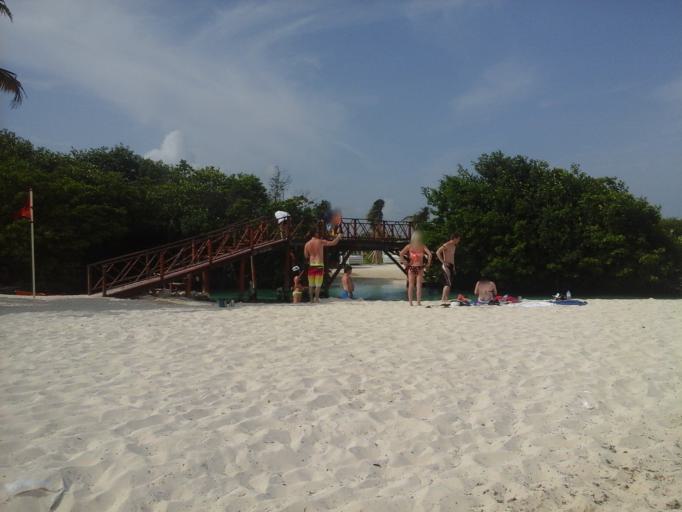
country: MX
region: Quintana Roo
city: Playa del Carmen
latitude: 20.7044
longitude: -87.0082
